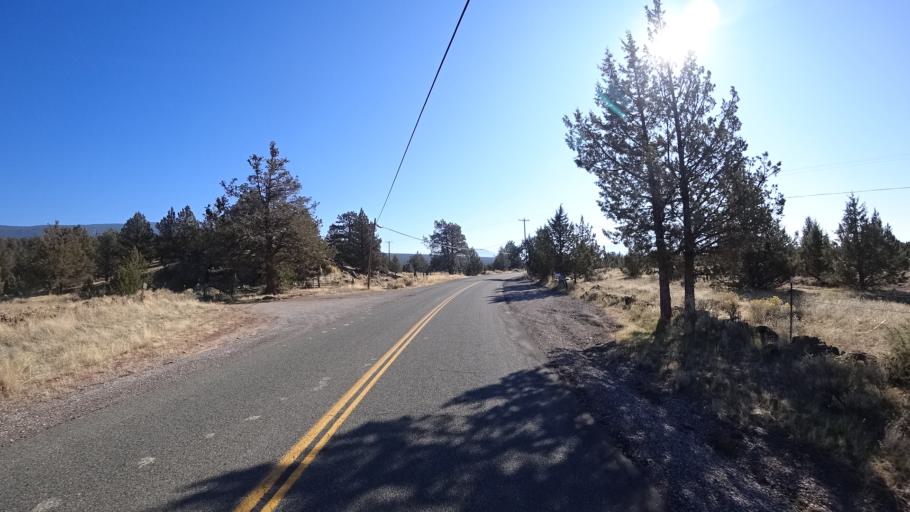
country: US
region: California
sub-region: Siskiyou County
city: Montague
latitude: 41.6403
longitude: -122.3427
